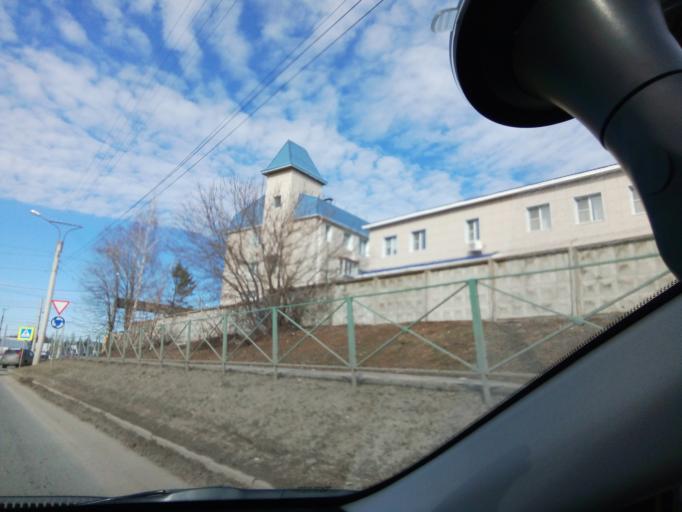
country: RU
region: Chuvashia
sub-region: Cheboksarskiy Rayon
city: Cheboksary
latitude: 56.1110
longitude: 47.2472
